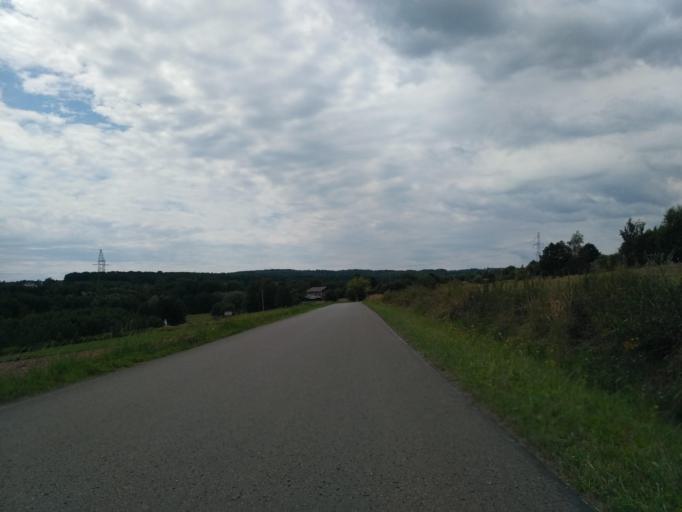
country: PL
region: Subcarpathian Voivodeship
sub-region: Powiat rzeszowski
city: Tyczyn
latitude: 49.9344
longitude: 22.0671
